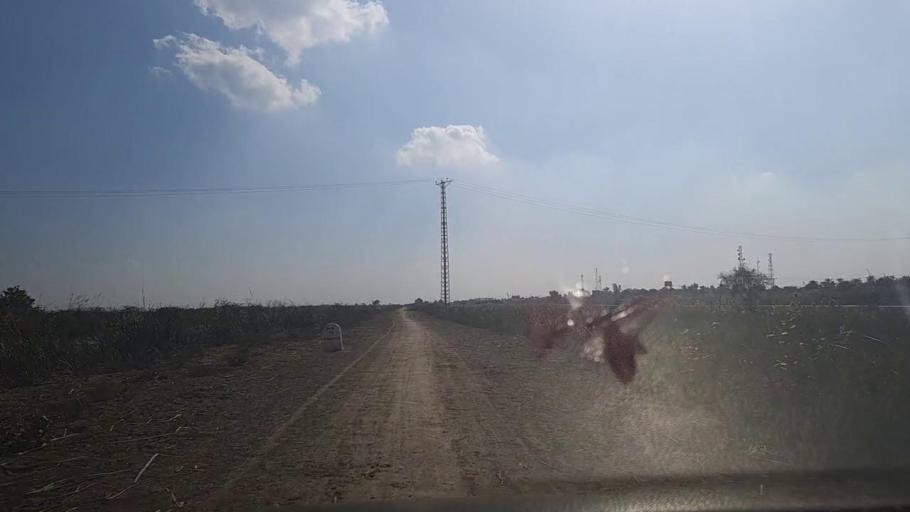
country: PK
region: Sindh
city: Tando Mittha Khan
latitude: 25.8066
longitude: 69.0733
